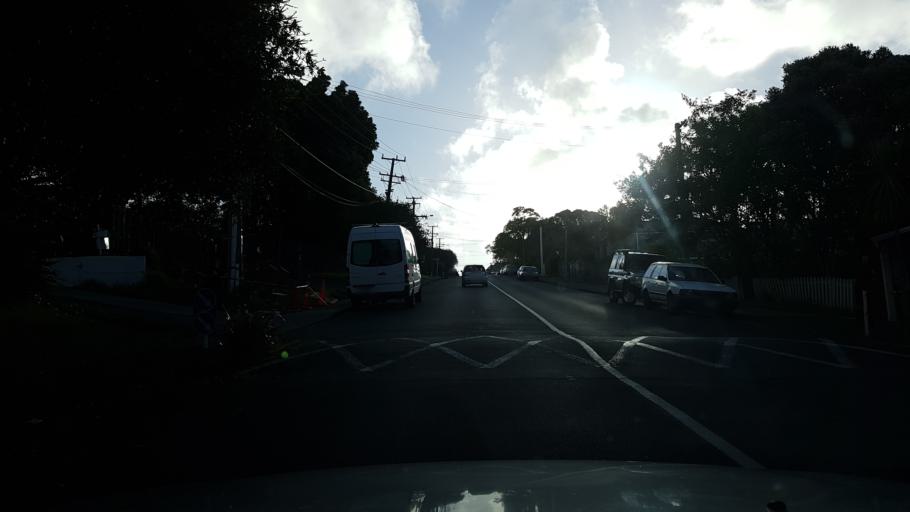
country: NZ
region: Auckland
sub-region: Auckland
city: North Shore
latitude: -36.8167
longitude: 174.7376
